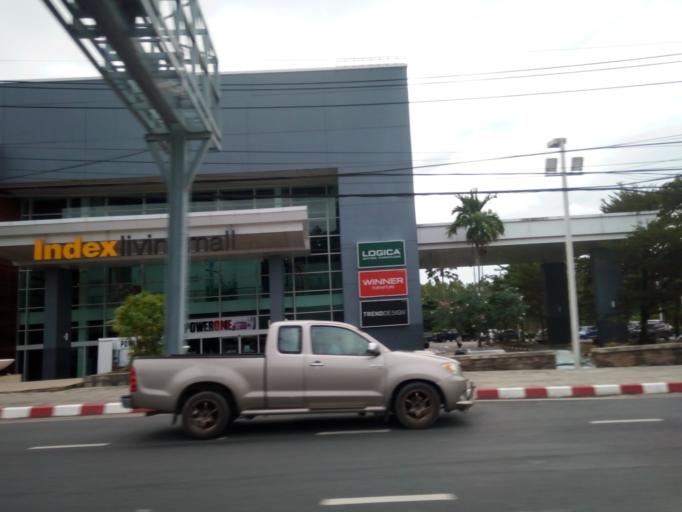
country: TH
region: Phuket
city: Wichit
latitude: 7.8969
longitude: 98.3682
